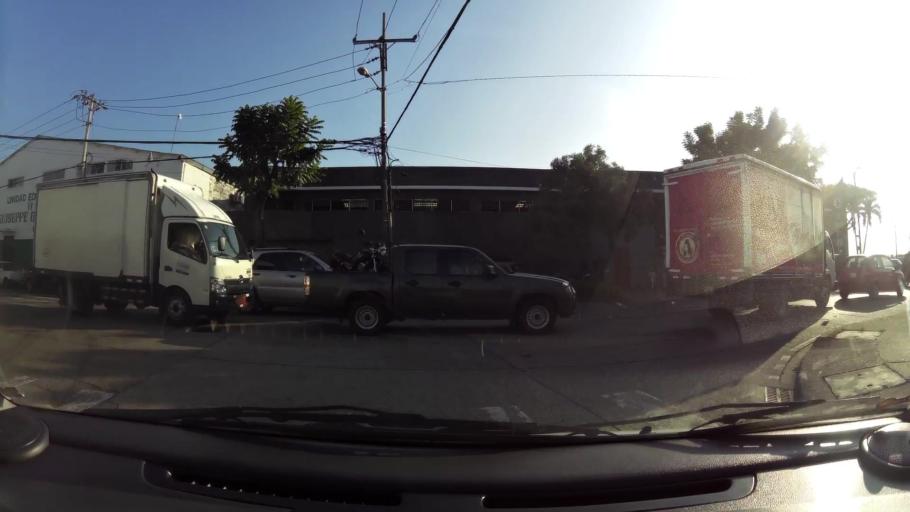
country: EC
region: Guayas
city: Eloy Alfaro
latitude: -2.1693
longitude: -79.8924
